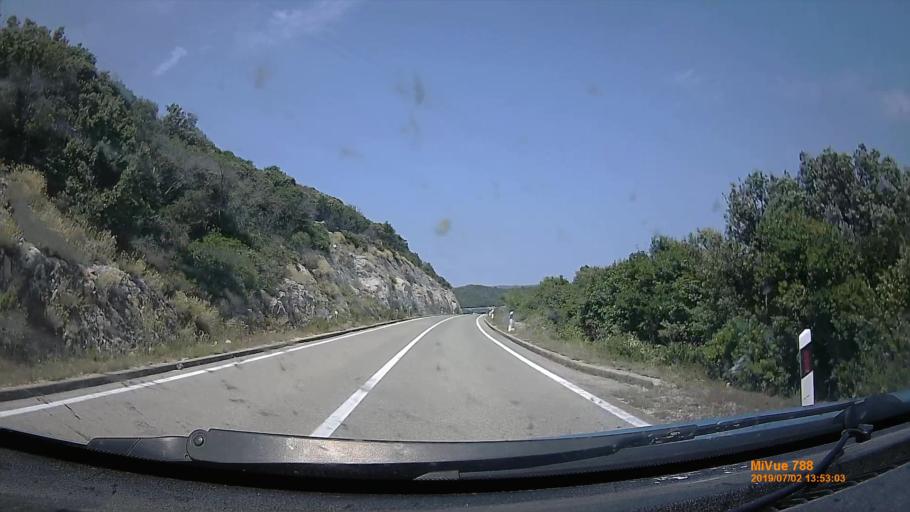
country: HR
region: Primorsko-Goranska
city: Mali Losinj
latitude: 44.6212
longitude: 14.3936
